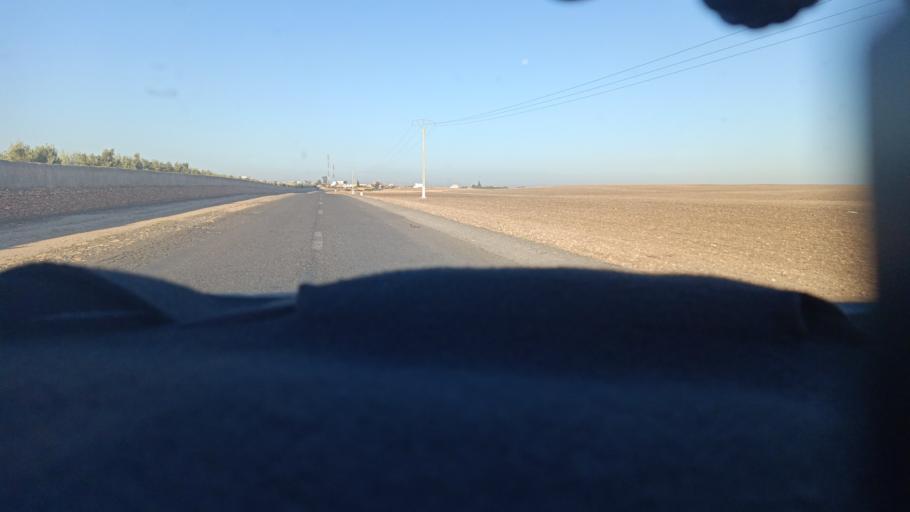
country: MA
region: Doukkala-Abda
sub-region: Safi
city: Youssoufia
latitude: 32.3709
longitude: -8.6675
